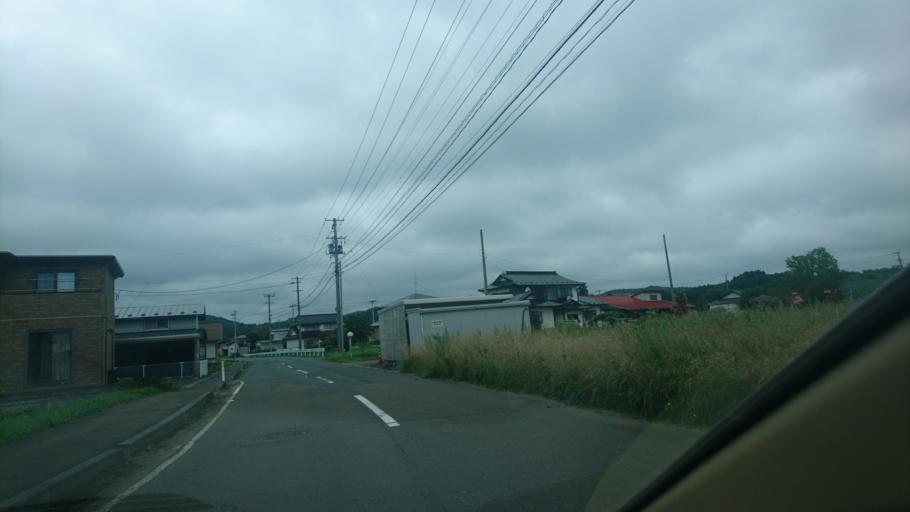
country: JP
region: Iwate
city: Kitakami
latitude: 39.2404
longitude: 141.1213
